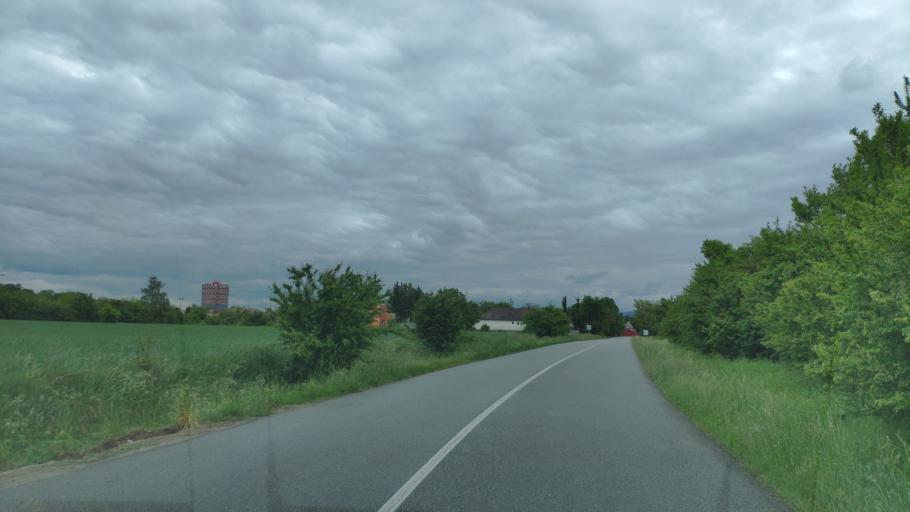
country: SK
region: Kosicky
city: Kosice
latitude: 48.5924
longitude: 21.1571
